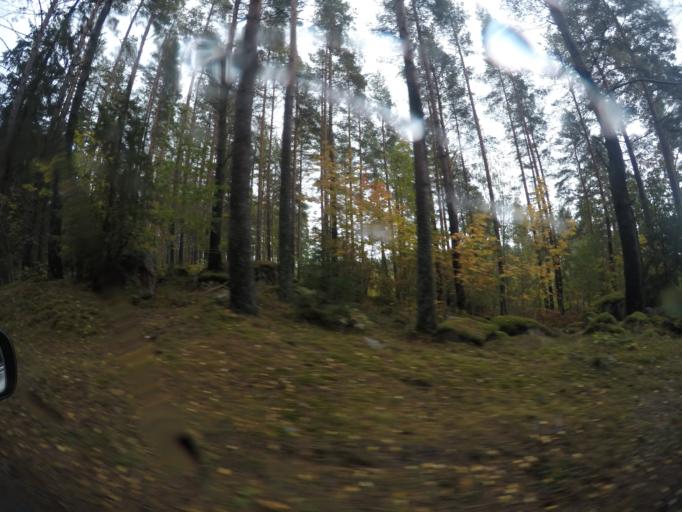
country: SE
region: Soedermanland
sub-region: Eskilstuna Kommun
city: Kvicksund
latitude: 59.3329
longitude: 16.2962
